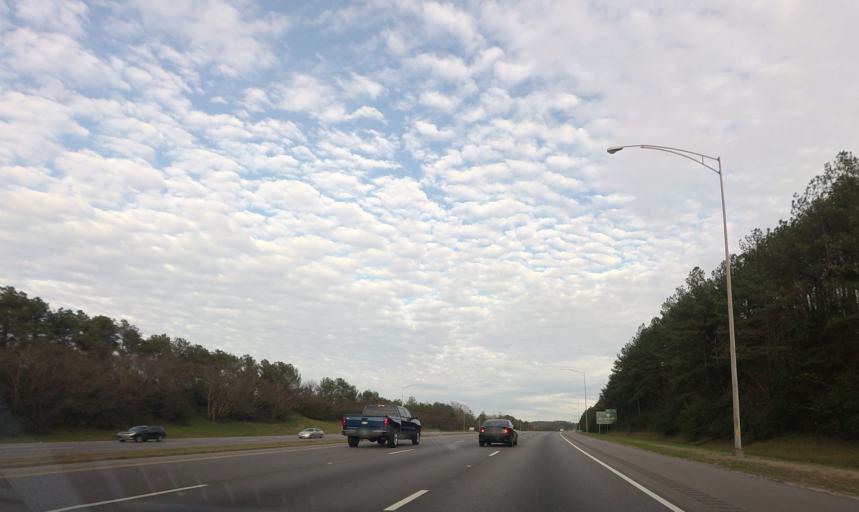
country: US
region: Alabama
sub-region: Jefferson County
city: Irondale
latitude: 33.5428
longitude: -86.6812
